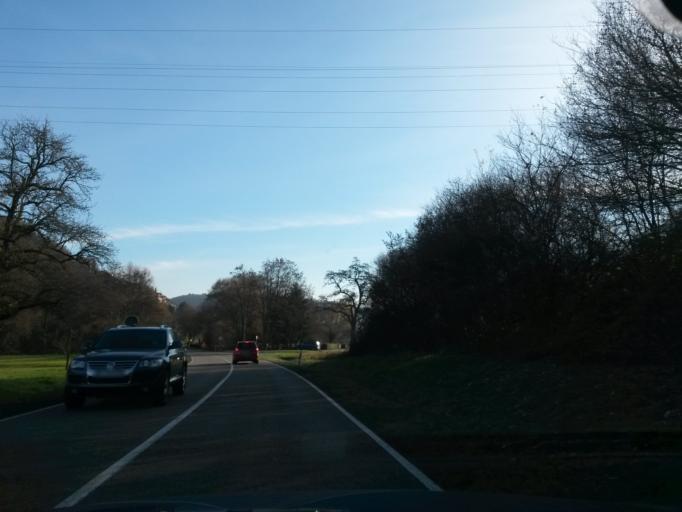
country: DE
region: Baden-Wuerttemberg
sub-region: Karlsruhe Region
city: Konigsbach-Stein
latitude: 48.9385
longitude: 8.6283
